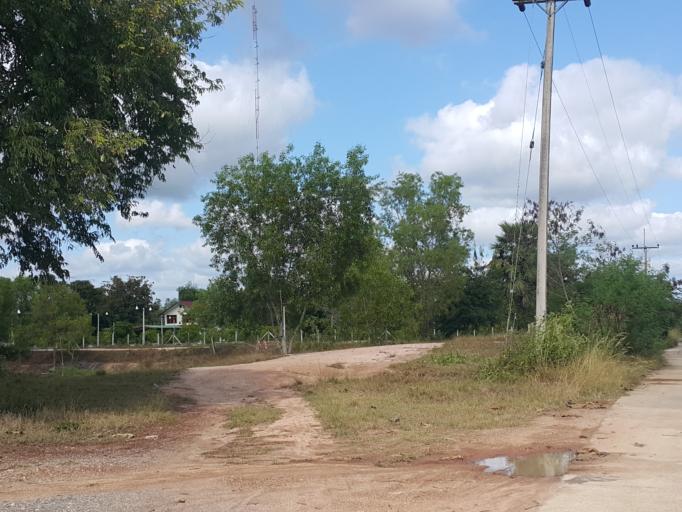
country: TH
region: Lampang
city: Hang Chat
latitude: 18.3423
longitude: 99.3597
